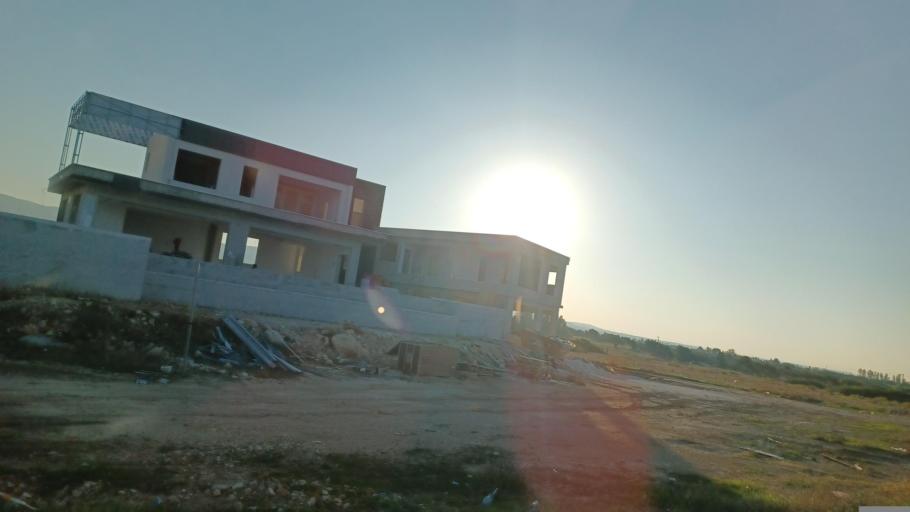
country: CY
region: Pafos
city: Pegeia
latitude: 34.8698
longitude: 32.3428
